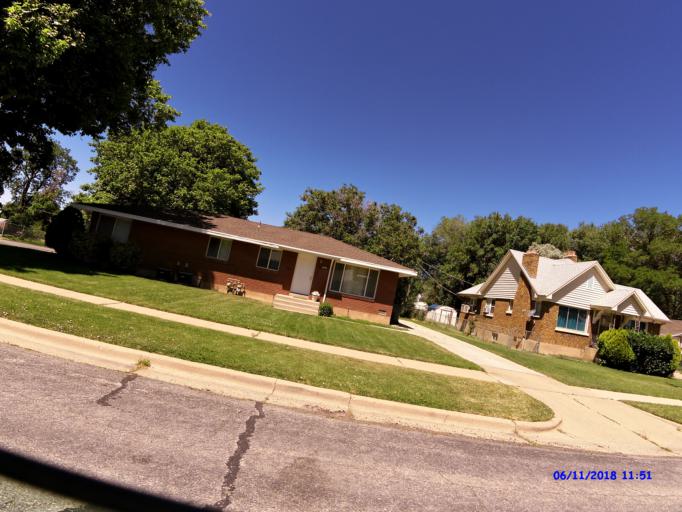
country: US
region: Utah
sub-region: Weber County
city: Ogden
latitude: 41.2331
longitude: -111.9521
